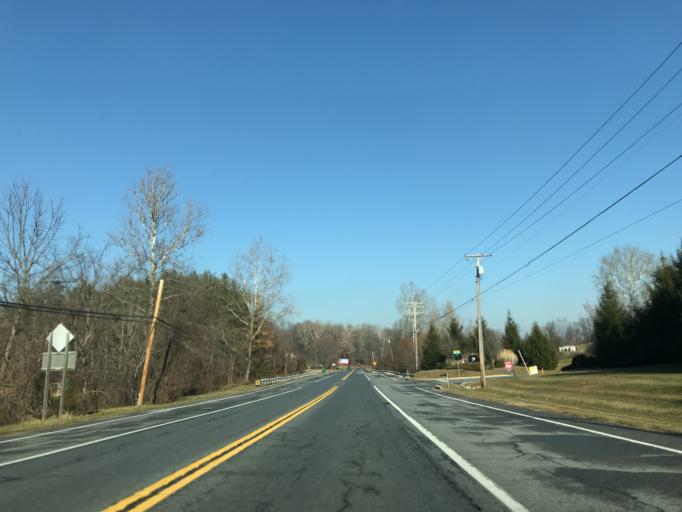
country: US
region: Maryland
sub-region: Carroll County
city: Westminster
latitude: 39.5353
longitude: -77.0211
